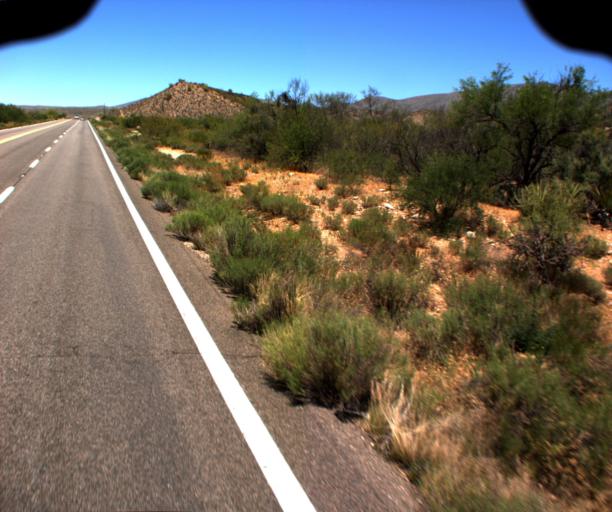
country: US
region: Arizona
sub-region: Pinal County
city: Kearny
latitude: 33.1317
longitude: -110.7816
